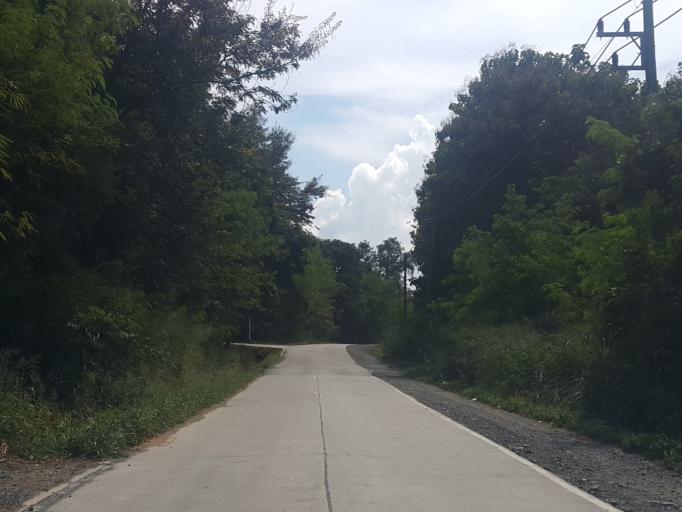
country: TH
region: Chiang Mai
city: Mae On
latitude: 18.8248
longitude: 99.2154
